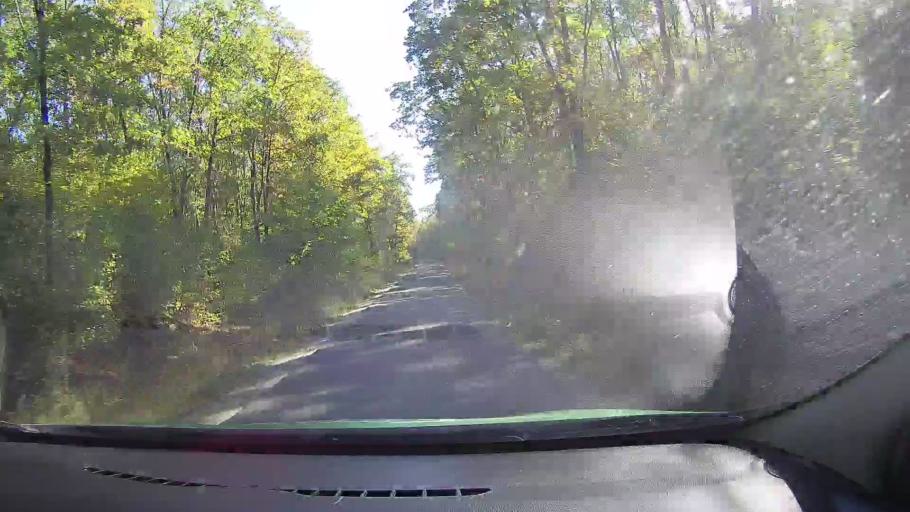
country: RO
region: Satu Mare
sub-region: Comuna Doba
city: Doba
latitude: 47.7096
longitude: 22.7533
